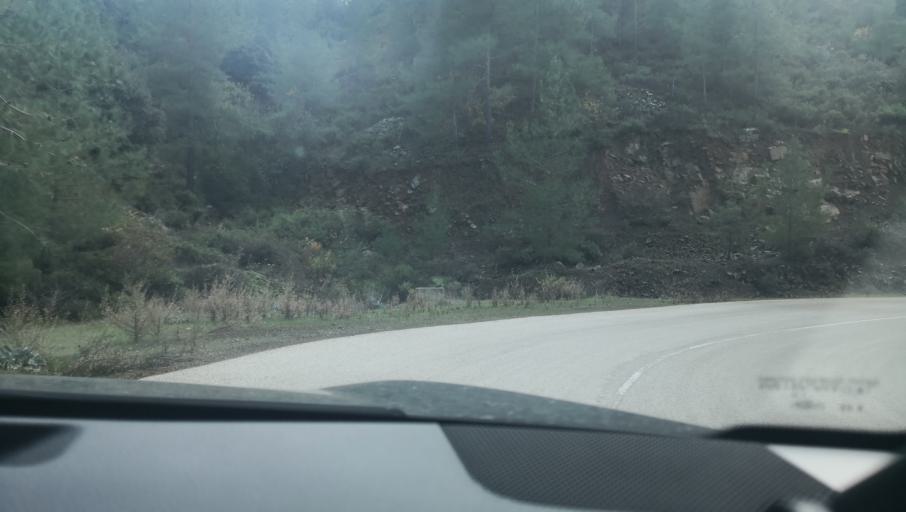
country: CY
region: Lefkosia
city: Lefka
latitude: 35.0517
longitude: 32.7463
